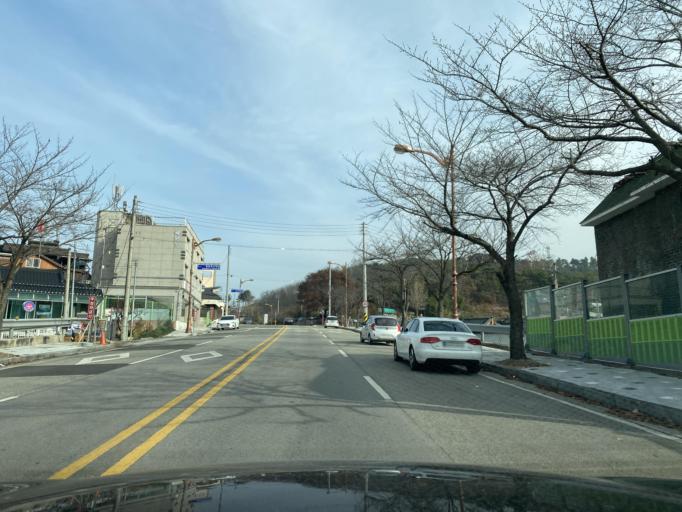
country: KR
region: Chungcheongnam-do
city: Yesan
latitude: 36.6827
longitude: 126.8350
